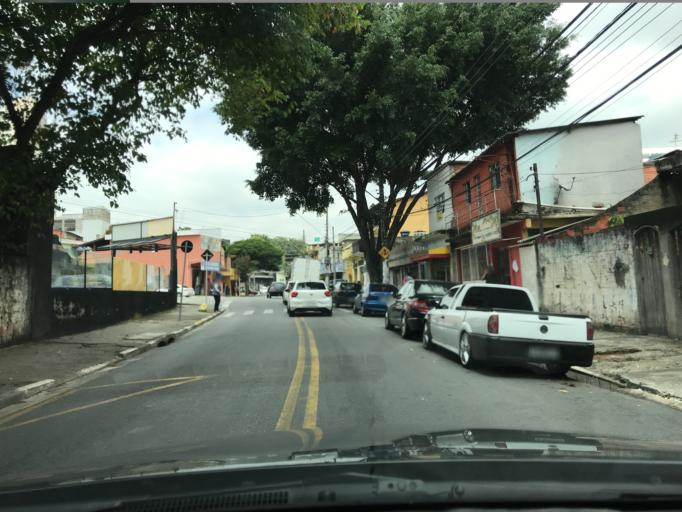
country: BR
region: Sao Paulo
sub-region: Barueri
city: Barueri
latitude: -23.5027
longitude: -46.8678
